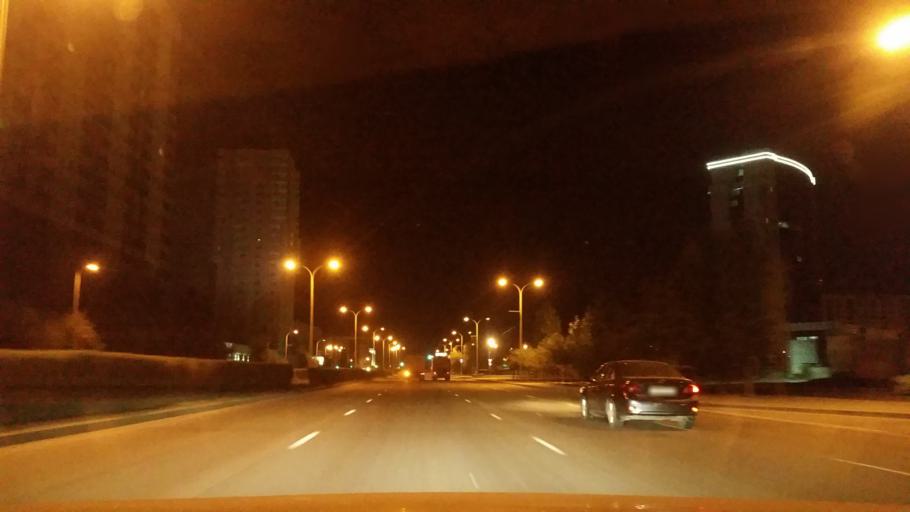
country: KZ
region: Astana Qalasy
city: Astana
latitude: 51.1182
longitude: 71.4607
